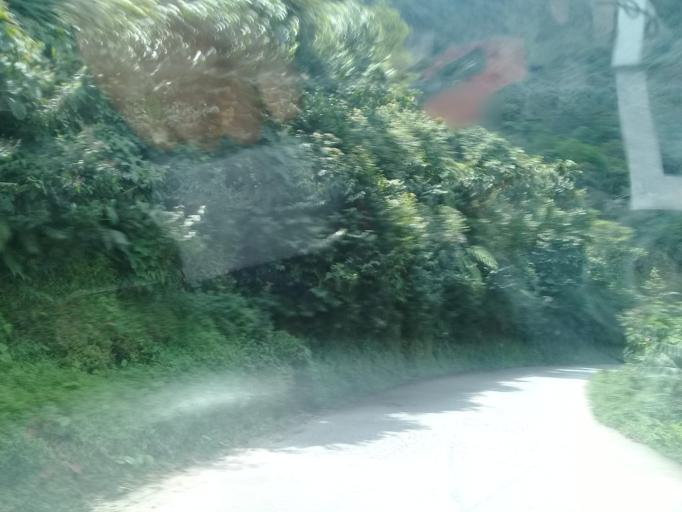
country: MX
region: Veracruz
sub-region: Tlilapan
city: Tonalixco
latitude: 18.7847
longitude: -97.0599
